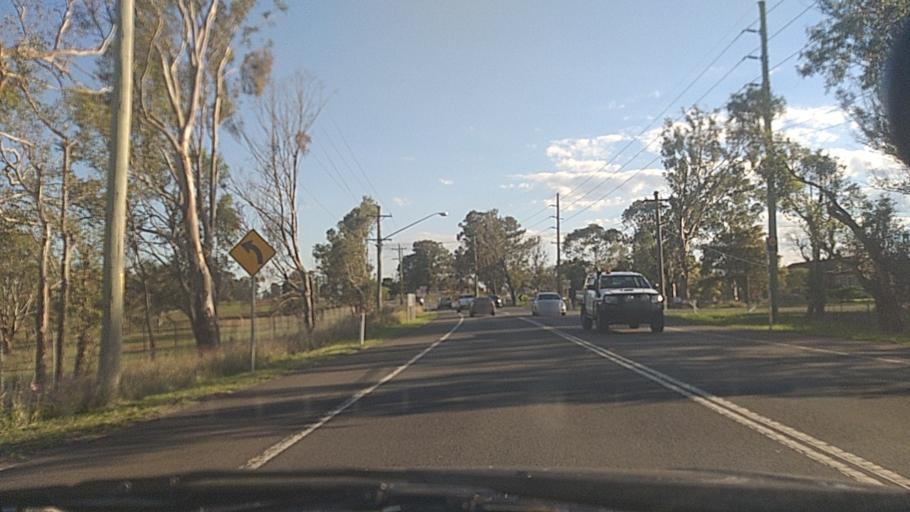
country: AU
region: New South Wales
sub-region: Penrith Municipality
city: Mulgoa
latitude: -33.8328
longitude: 150.6831
